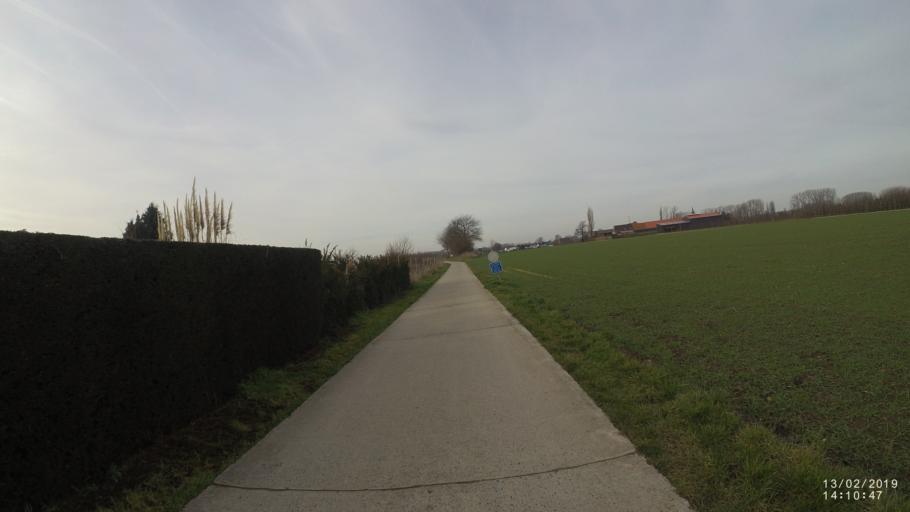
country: BE
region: Flanders
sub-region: Provincie Vlaams-Brabant
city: Zoutleeuw
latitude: 50.8185
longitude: 5.1311
